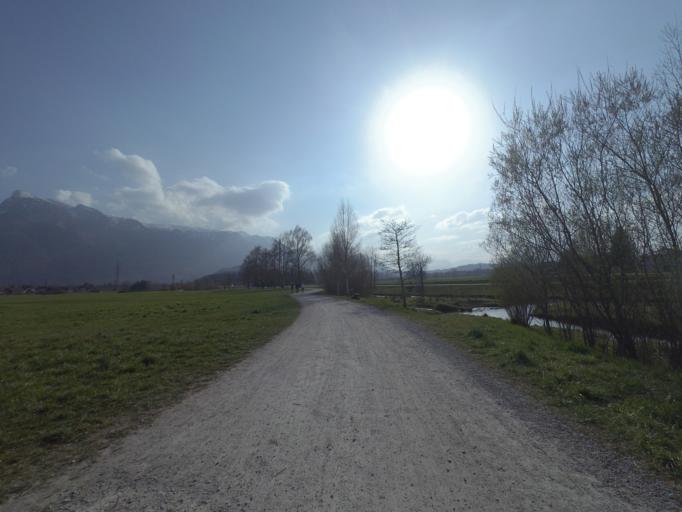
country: AT
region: Salzburg
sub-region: Politischer Bezirk Salzburg-Umgebung
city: Grodig
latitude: 47.7712
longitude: 13.0023
